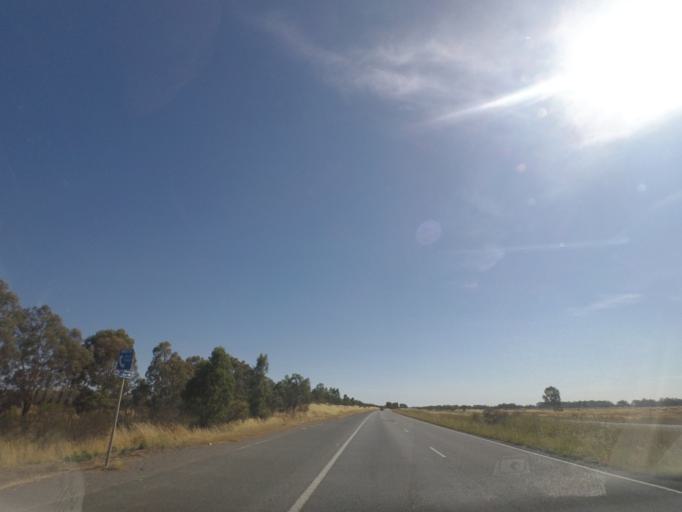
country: AU
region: Victoria
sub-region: Greater Shepparton
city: Shepparton
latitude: -36.6659
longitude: 145.2734
